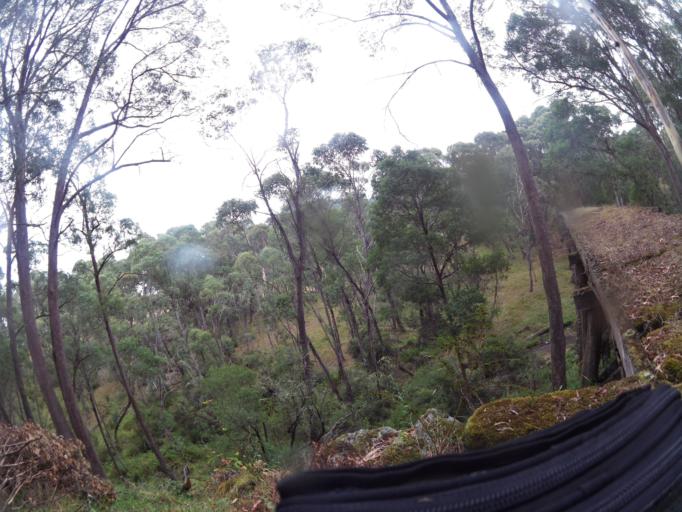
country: AU
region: New South Wales
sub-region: Greater Hume Shire
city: Holbrook
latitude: -36.2318
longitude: 147.6016
